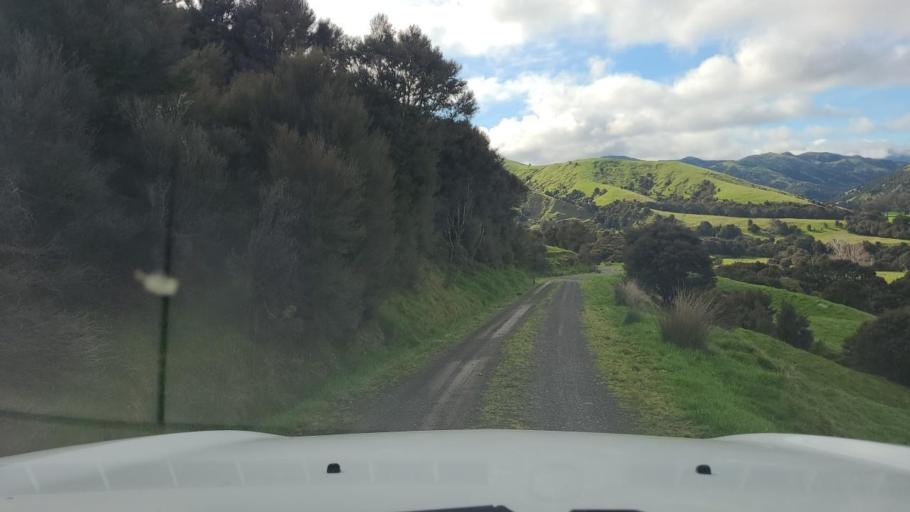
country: NZ
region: Wellington
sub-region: South Wairarapa District
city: Waipawa
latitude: -41.2585
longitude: 175.6881
